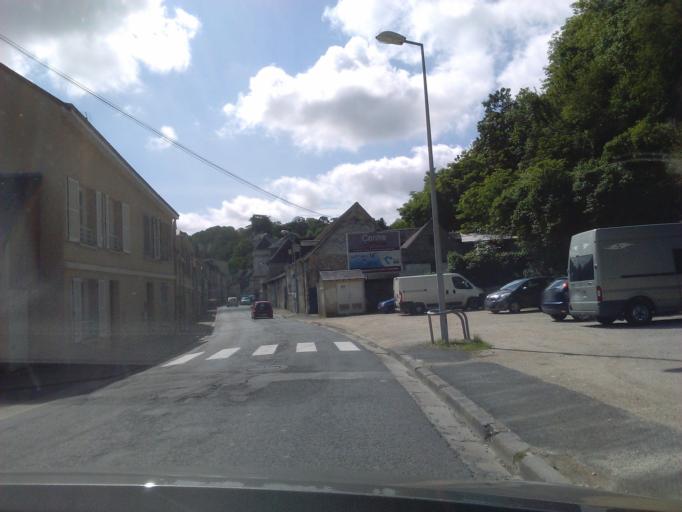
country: FR
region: Centre
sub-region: Departement du Loir-et-Cher
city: Vendome
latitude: 47.7917
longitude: 1.0611
